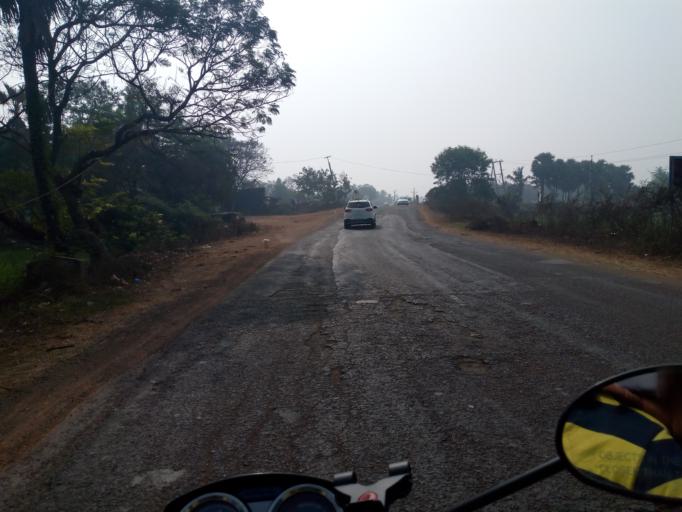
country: IN
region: Andhra Pradesh
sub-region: West Godavari
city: Tadepallegudem
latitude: 16.7987
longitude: 81.4141
